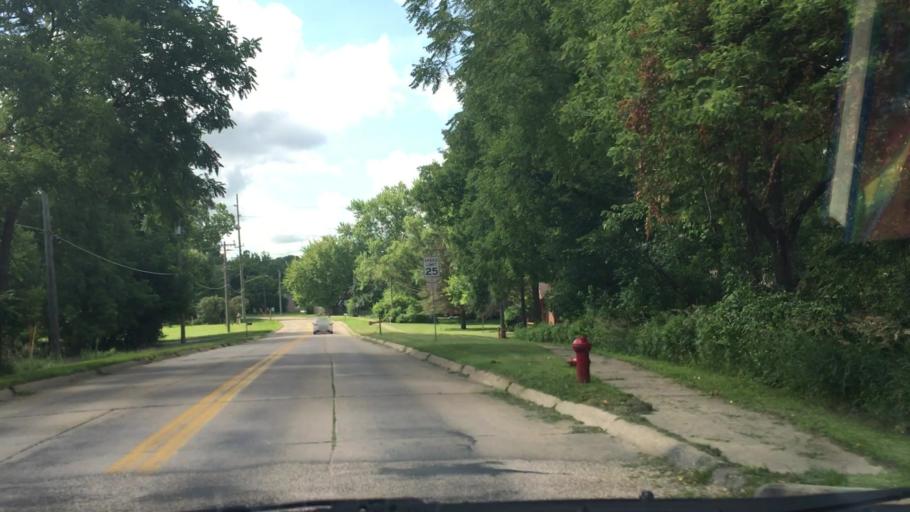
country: US
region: Iowa
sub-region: Johnson County
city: Iowa City
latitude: 41.6870
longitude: -91.5244
